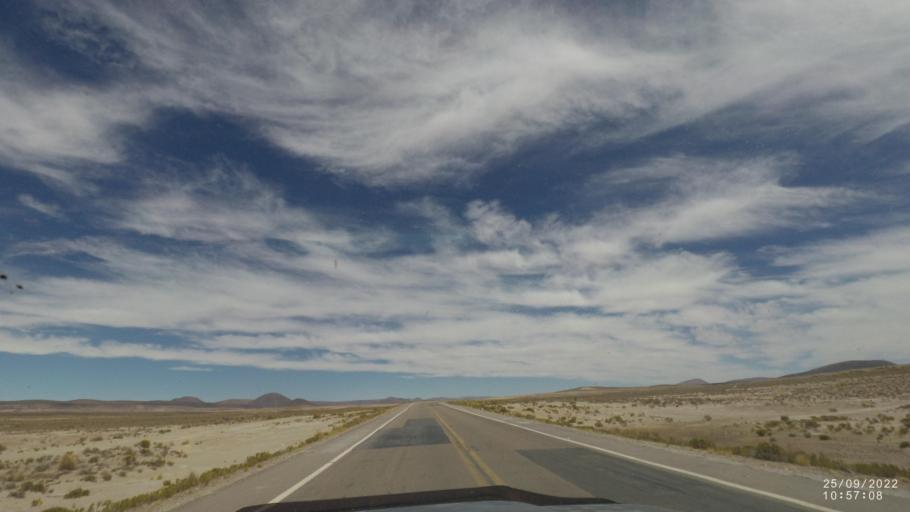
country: BO
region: Oruro
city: Challapata
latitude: -19.4774
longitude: -66.8859
